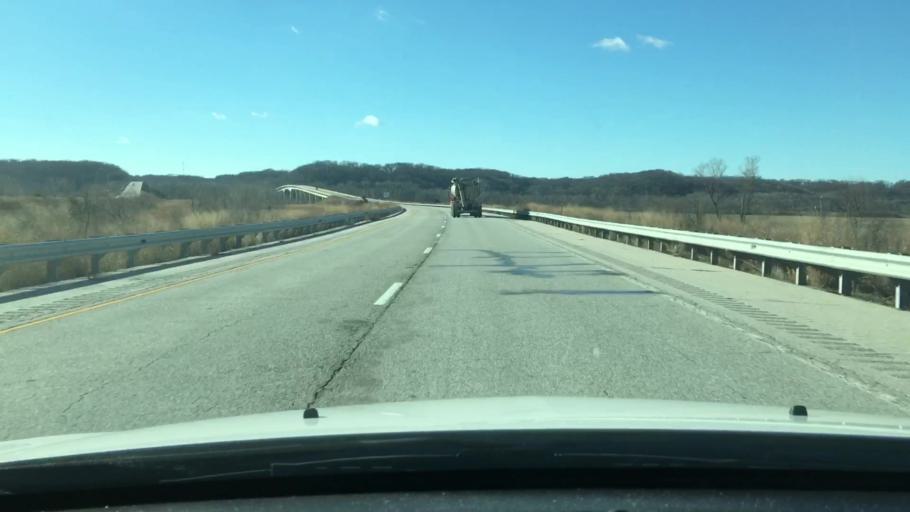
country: US
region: Illinois
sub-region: Pike County
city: Griggsville
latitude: 39.6920
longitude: -90.6276
